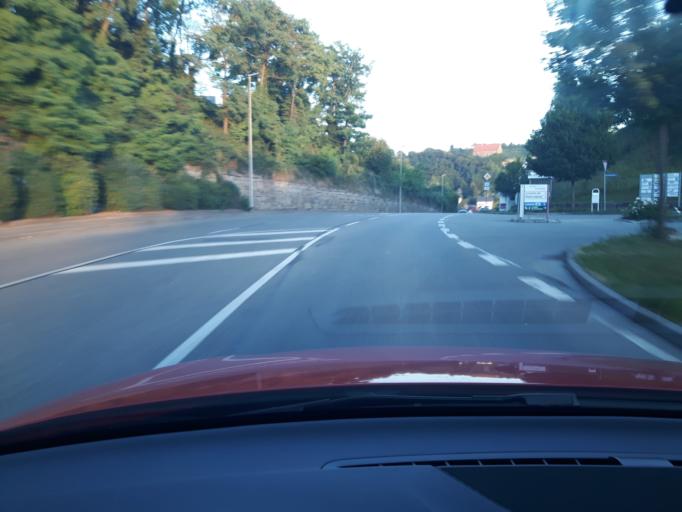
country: DE
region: Baden-Wuerttemberg
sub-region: Regierungsbezirk Stuttgart
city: Cleebronn
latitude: 49.0469
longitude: 9.0352
